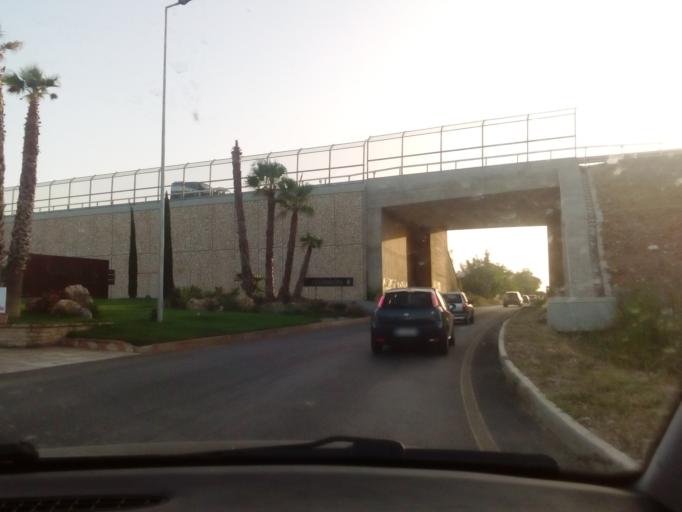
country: IT
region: Apulia
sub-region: Provincia di Bari
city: Altamura
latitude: 40.8423
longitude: 16.5746
